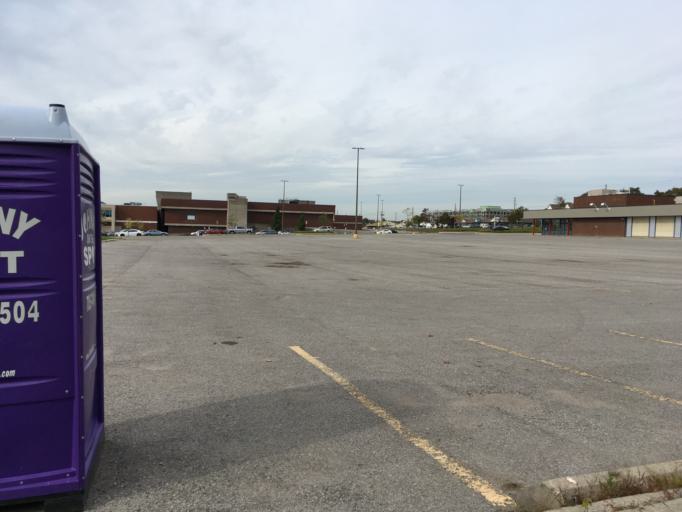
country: CA
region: Ontario
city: Oshawa
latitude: 43.8930
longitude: -78.8779
